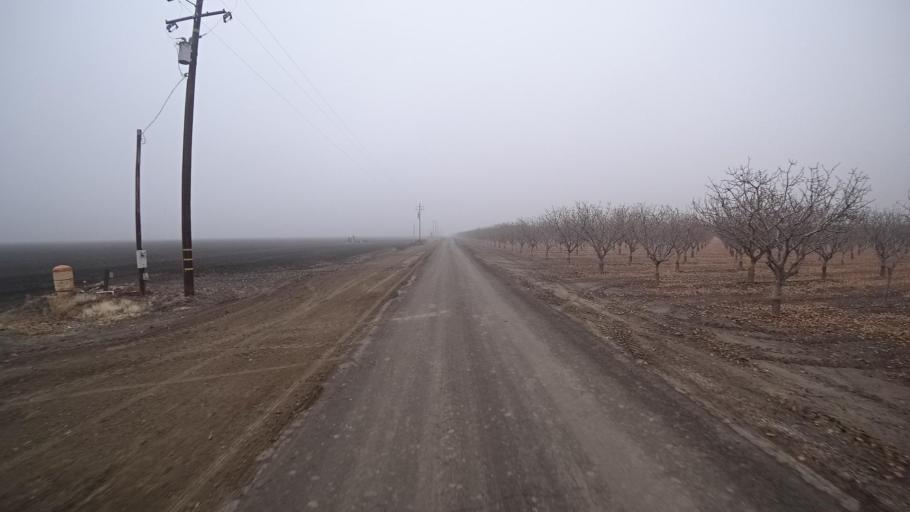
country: US
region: California
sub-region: Kern County
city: Buttonwillow
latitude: 35.4268
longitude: -119.5583
